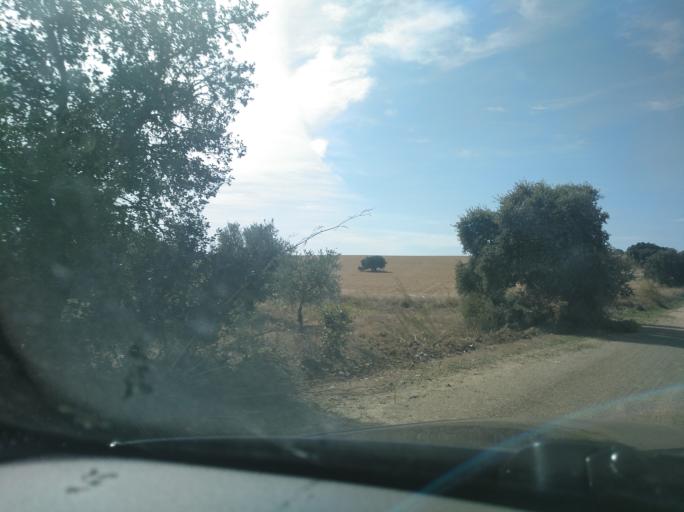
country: PT
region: Portalegre
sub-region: Campo Maior
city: Campo Maior
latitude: 39.0483
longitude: -7.0539
